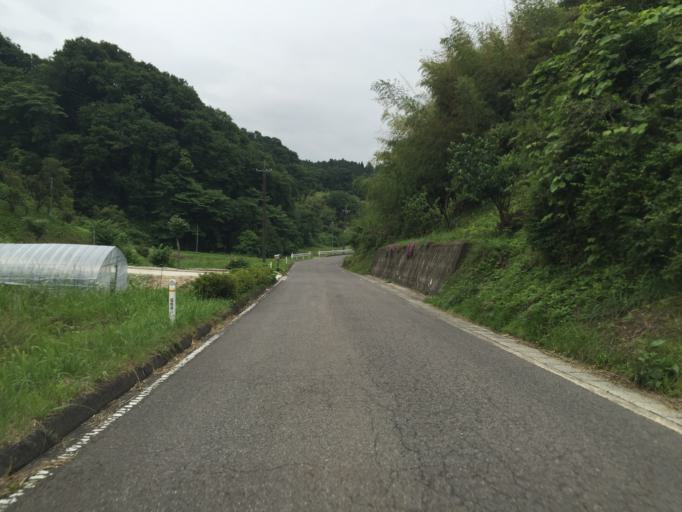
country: JP
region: Fukushima
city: Nihommatsu
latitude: 37.6304
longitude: 140.5615
